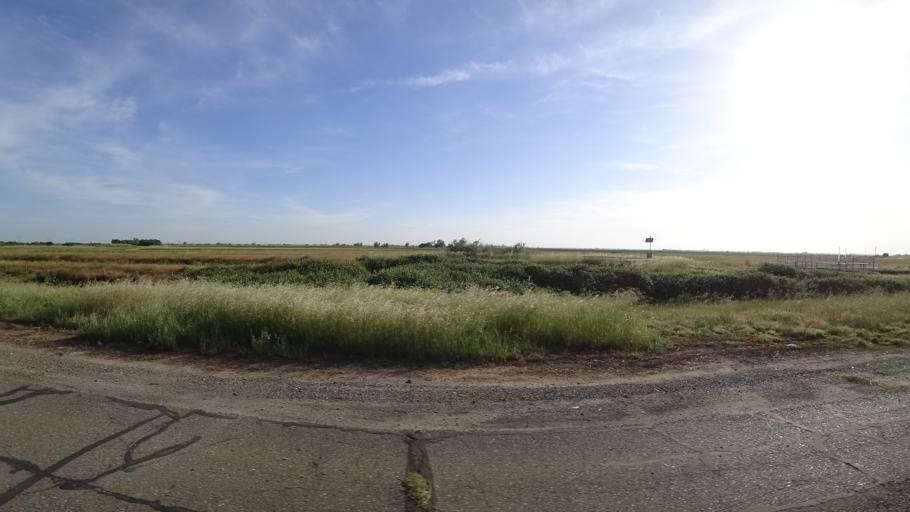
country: US
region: California
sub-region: Yuba County
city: Plumas Lake
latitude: 39.0485
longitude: -121.4904
